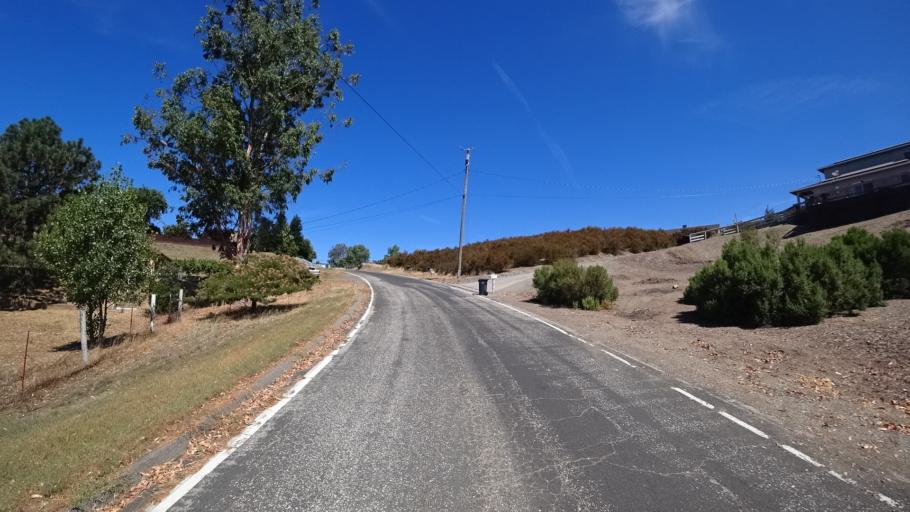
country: US
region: California
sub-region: Calaveras County
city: Valley Springs
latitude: 38.1547
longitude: -120.8323
